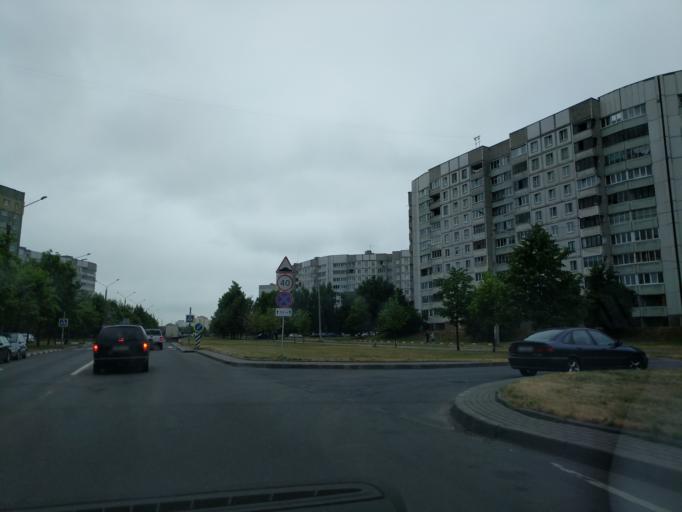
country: BY
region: Minsk
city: Malinovka
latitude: 53.8588
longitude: 27.4606
